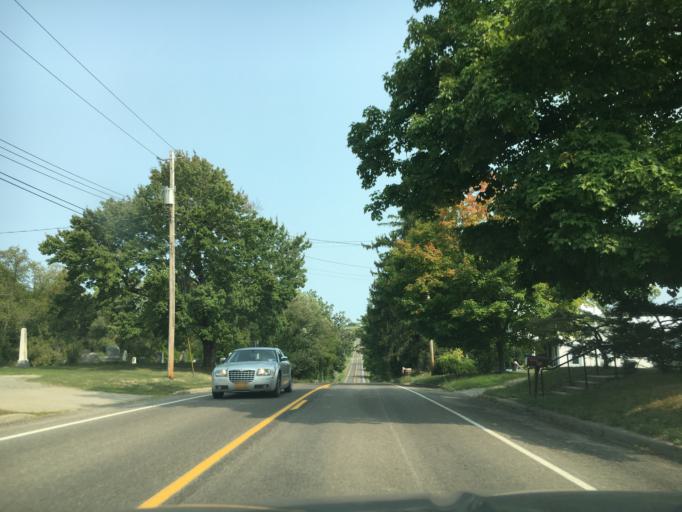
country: US
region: New York
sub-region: Steuben County
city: Sylvan Beach
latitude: 42.4710
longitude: -77.1028
